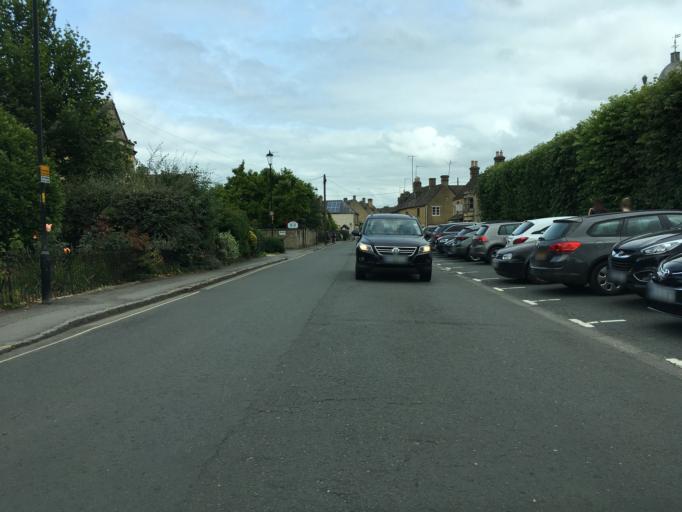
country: GB
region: England
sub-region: Gloucestershire
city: Bourton on the Water
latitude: 51.8854
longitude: -1.7587
